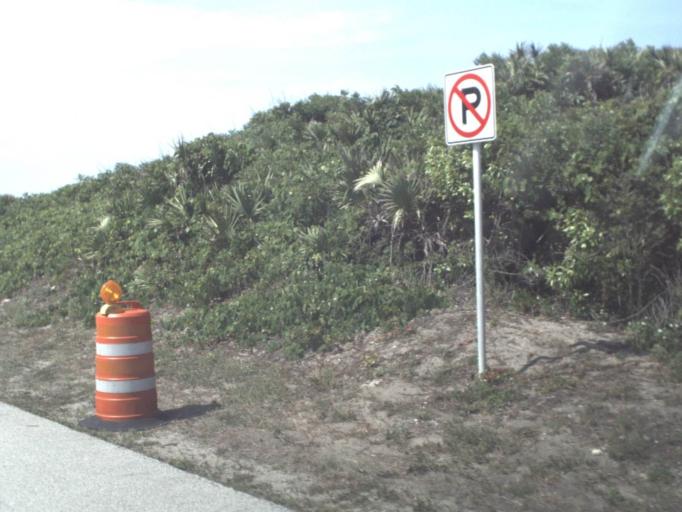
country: US
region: Florida
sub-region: Saint Johns County
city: Palm Valley
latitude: 30.0735
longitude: -81.3350
